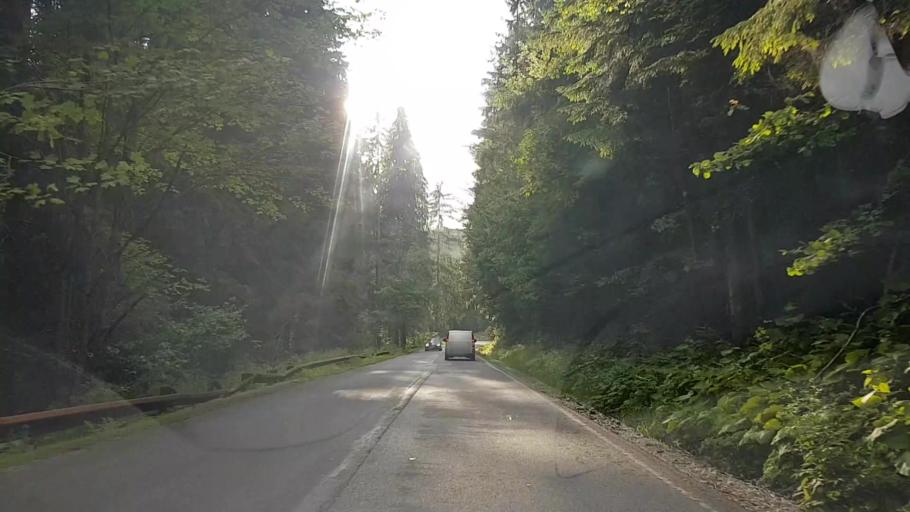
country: RO
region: Harghita
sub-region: Comuna Remetea
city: Remetea
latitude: 46.6739
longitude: 25.3417
